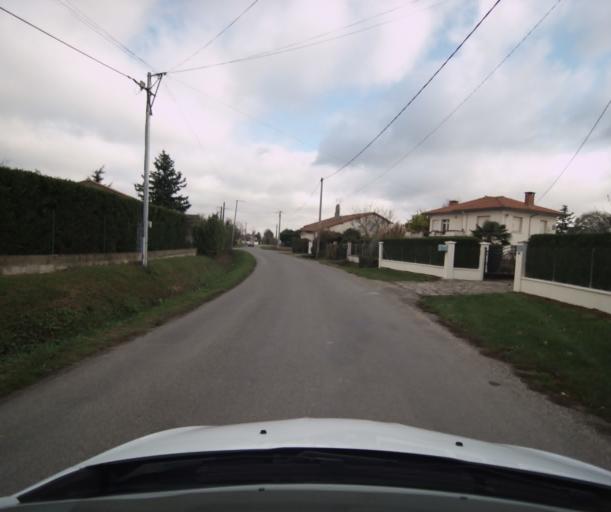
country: FR
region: Midi-Pyrenees
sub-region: Departement du Tarn-et-Garonne
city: Castelsarrasin
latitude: 44.0387
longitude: 1.1226
